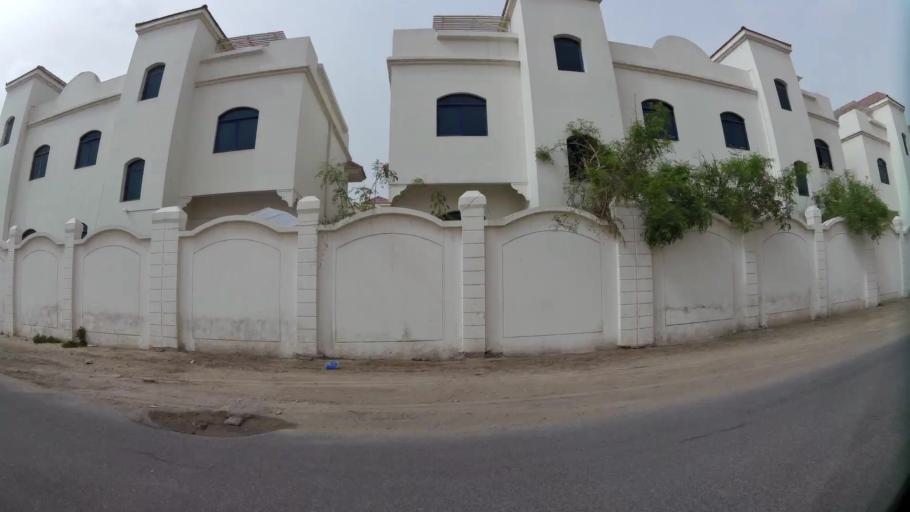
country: QA
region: Baladiyat ad Dawhah
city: Doha
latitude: 25.2522
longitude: 51.5298
